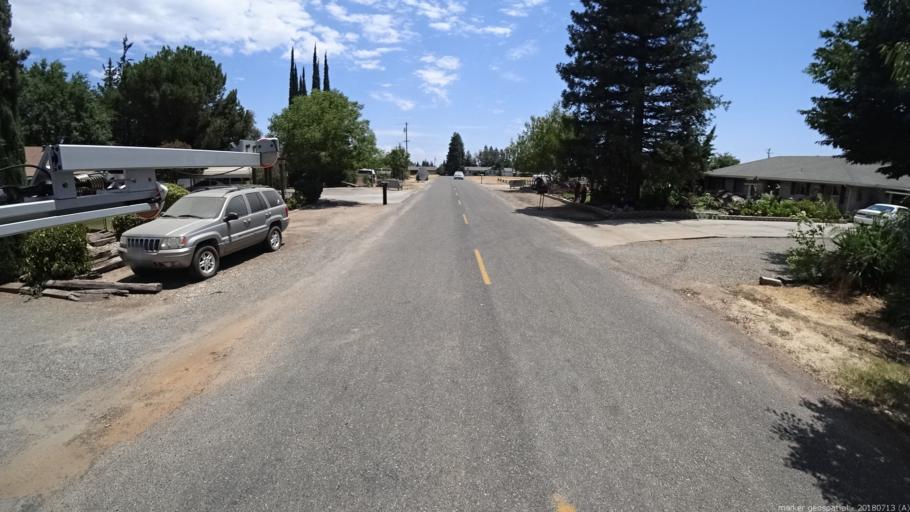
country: US
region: California
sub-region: Madera County
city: Madera Acres
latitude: 36.9951
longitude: -120.0781
